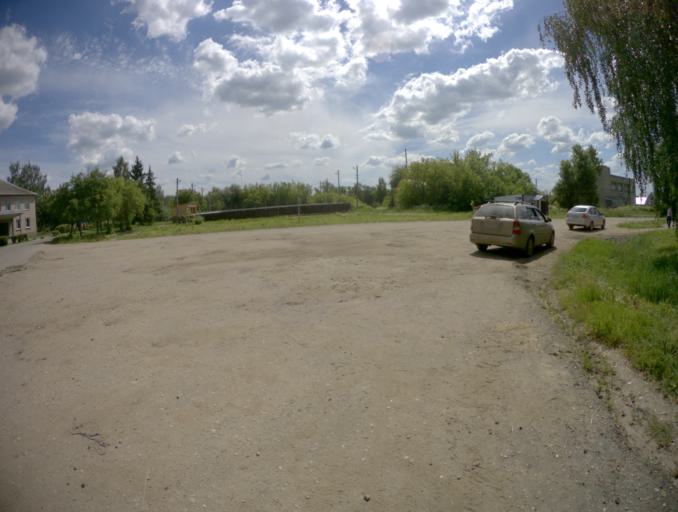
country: RU
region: Vladimir
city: Stavrovo
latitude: 56.3644
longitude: 39.9926
